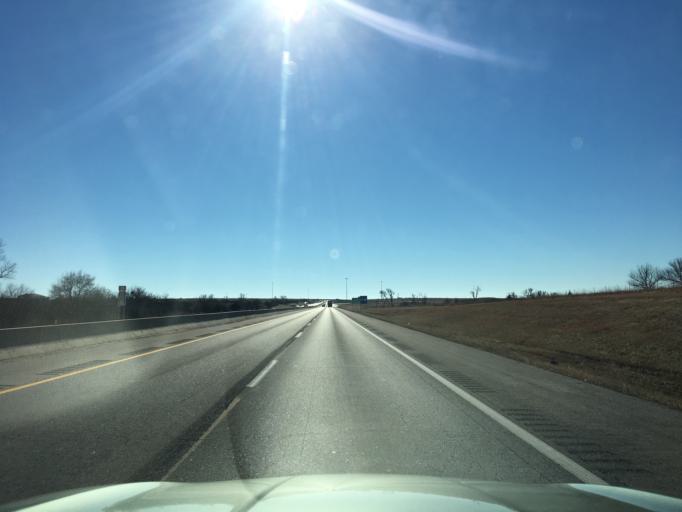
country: US
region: Kansas
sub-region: Sumner County
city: Wellington
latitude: 37.0667
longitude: -97.3385
